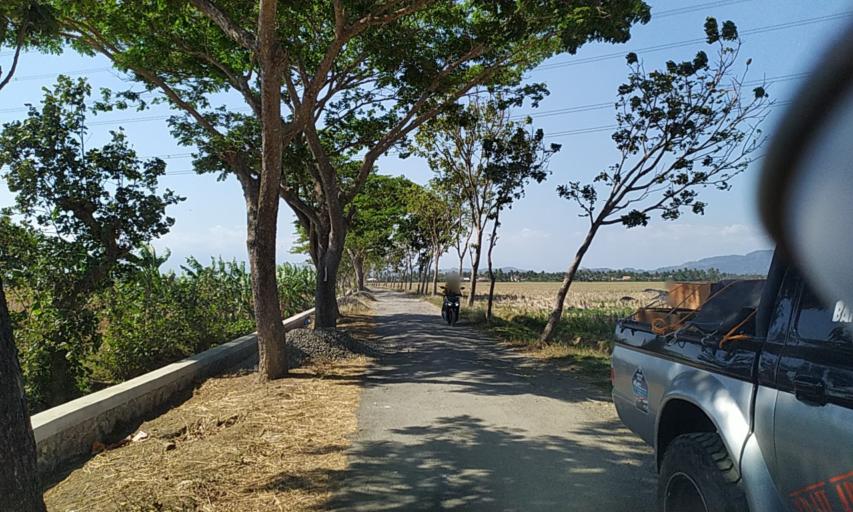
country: ID
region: Central Java
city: Mernek
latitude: -7.6036
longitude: 109.1708
